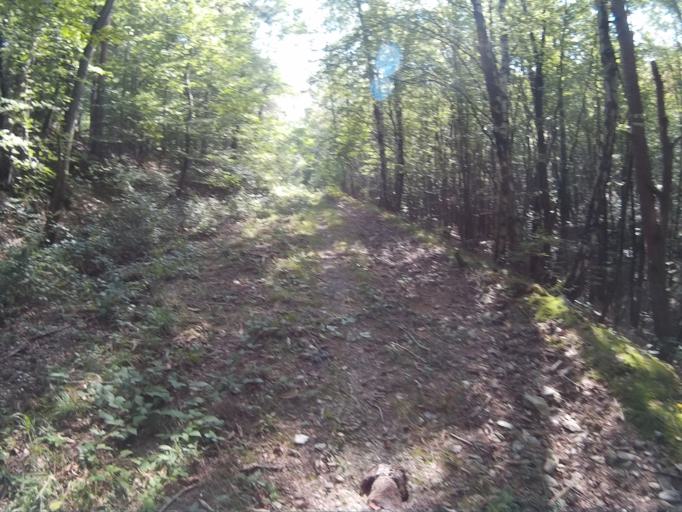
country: AT
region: Burgenland
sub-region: Politischer Bezirk Oberpullendorf
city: Mannersdorf an der Rabnitz
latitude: 47.4043
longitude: 16.5082
